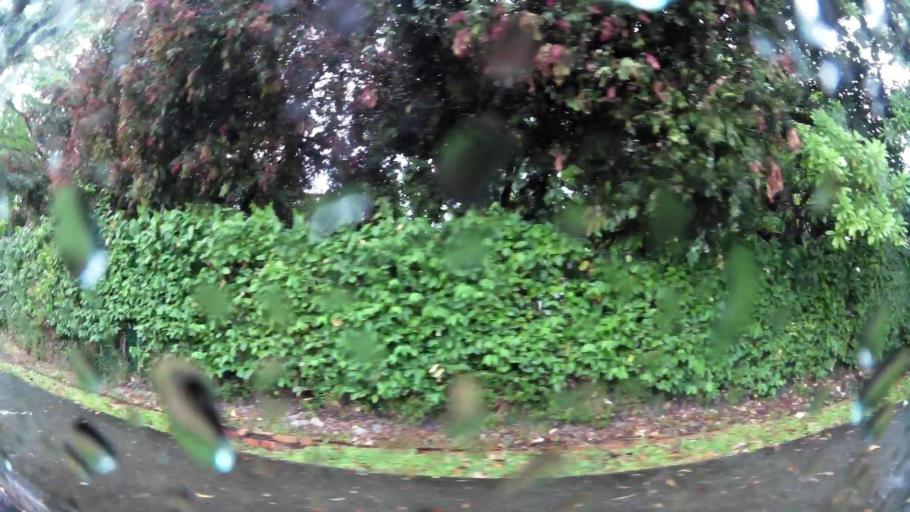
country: SG
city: Singapore
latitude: 1.3393
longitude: 103.8775
